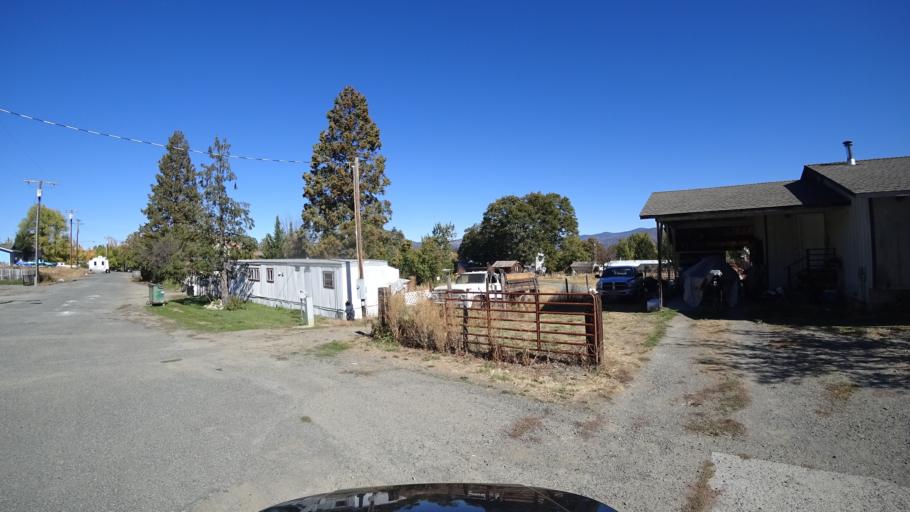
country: US
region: California
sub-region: Siskiyou County
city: Yreka
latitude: 41.4534
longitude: -122.9007
